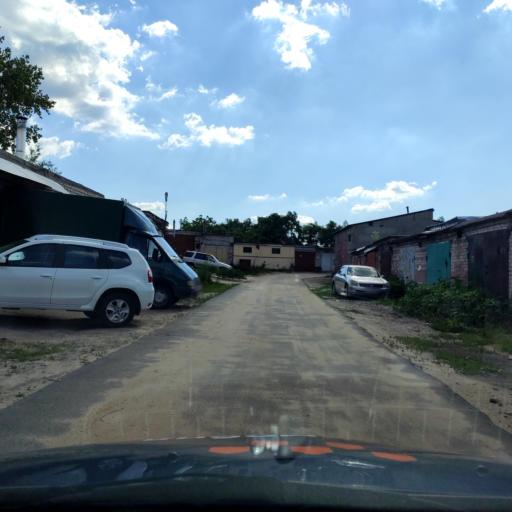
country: RU
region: Voronezj
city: Pridonskoy
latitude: 51.6341
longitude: 39.1228
